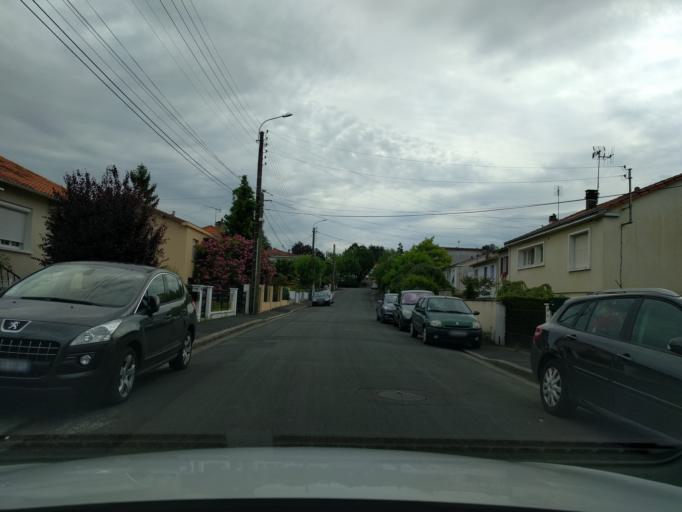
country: FR
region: Poitou-Charentes
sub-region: Departement des Deux-Sevres
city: Niort
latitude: 46.3176
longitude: -0.4417
